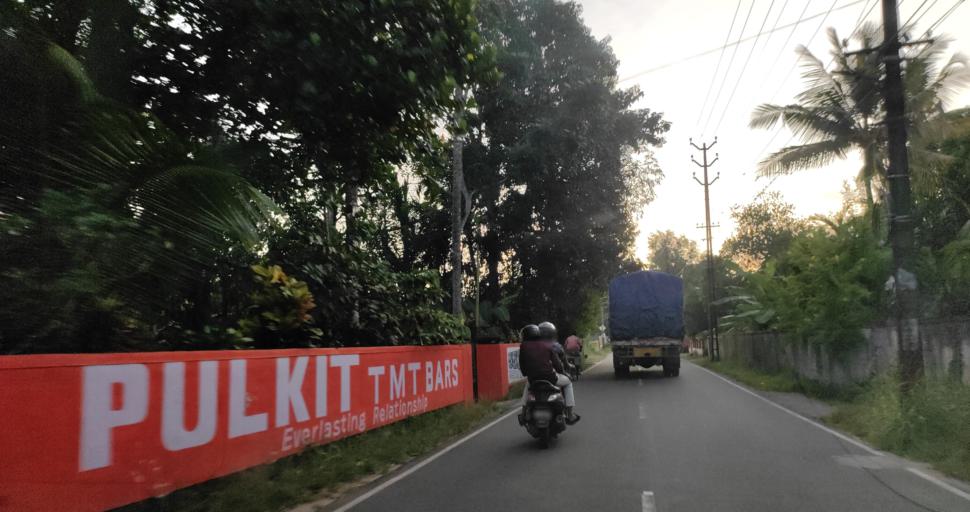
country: IN
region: Kerala
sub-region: Alappuzha
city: Shertallai
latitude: 9.6408
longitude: 76.3510
